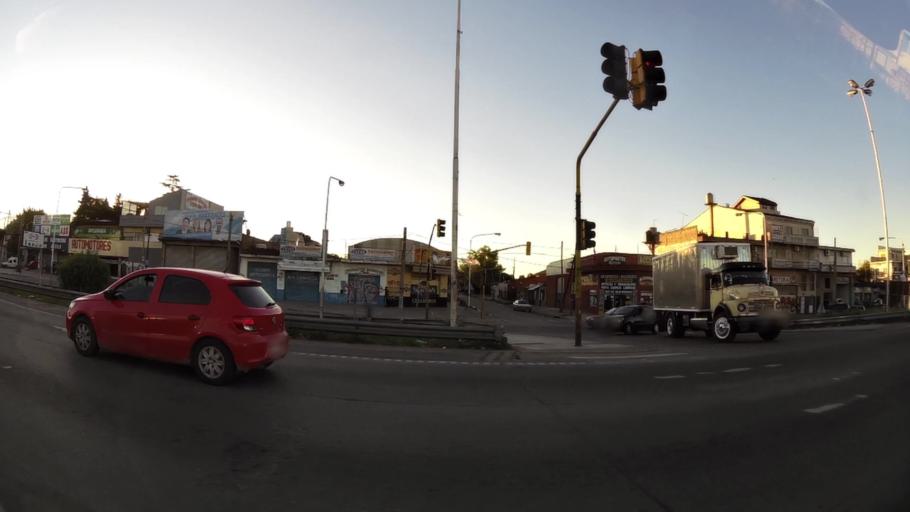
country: AR
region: Buenos Aires
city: Pontevedra
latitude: -34.7695
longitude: -58.6196
